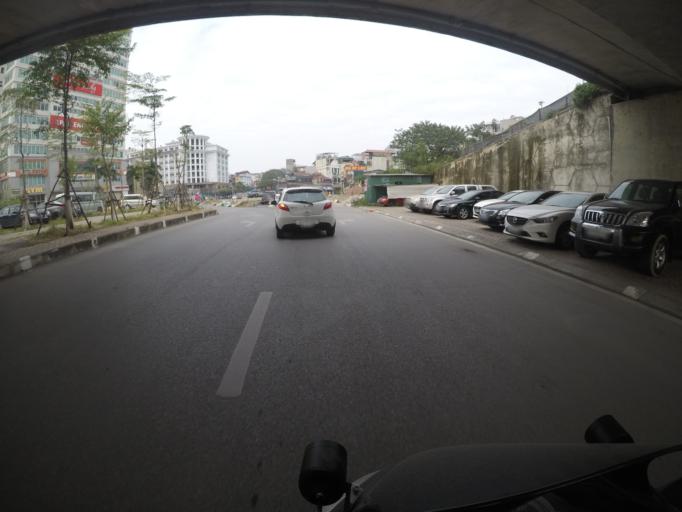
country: VN
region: Ha Noi
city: Cau Giay
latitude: 21.0424
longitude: 105.8169
